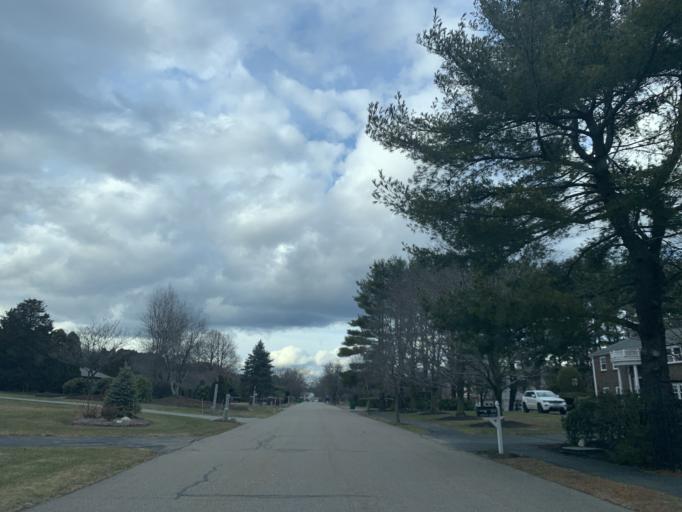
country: US
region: Massachusetts
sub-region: Norfolk County
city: Dedham
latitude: 42.2088
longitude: -71.1611
